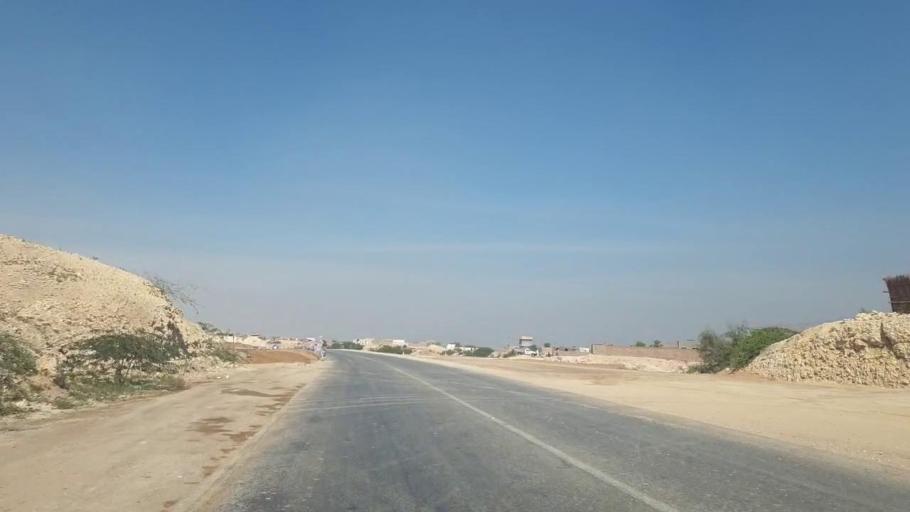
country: PK
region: Sindh
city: Hala
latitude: 25.7302
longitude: 68.2929
